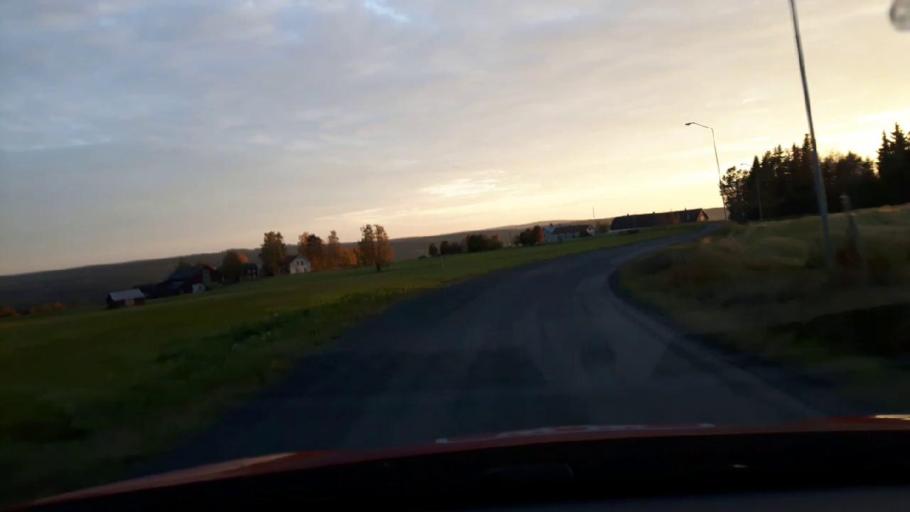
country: SE
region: Jaemtland
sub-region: OEstersunds Kommun
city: Lit
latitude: 63.2879
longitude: 14.7894
